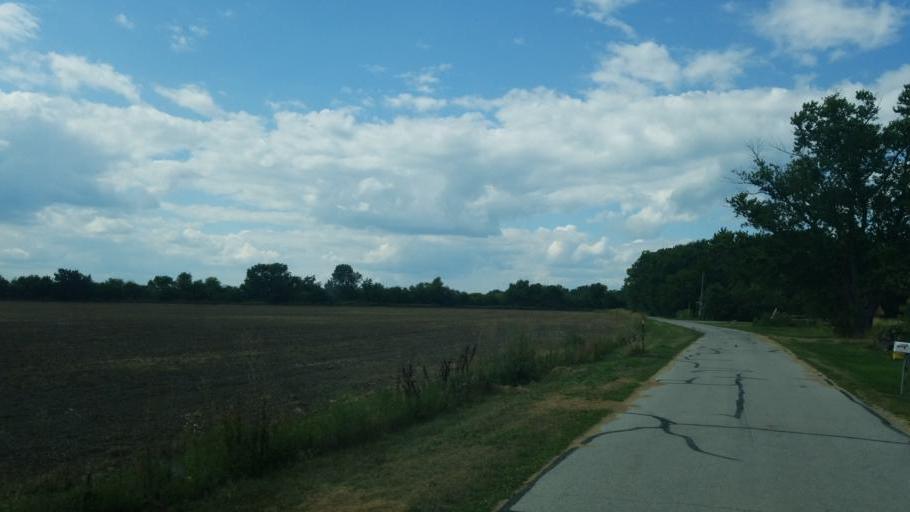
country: US
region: Ohio
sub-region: Lucas County
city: Curtice
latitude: 41.6546
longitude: -83.2497
